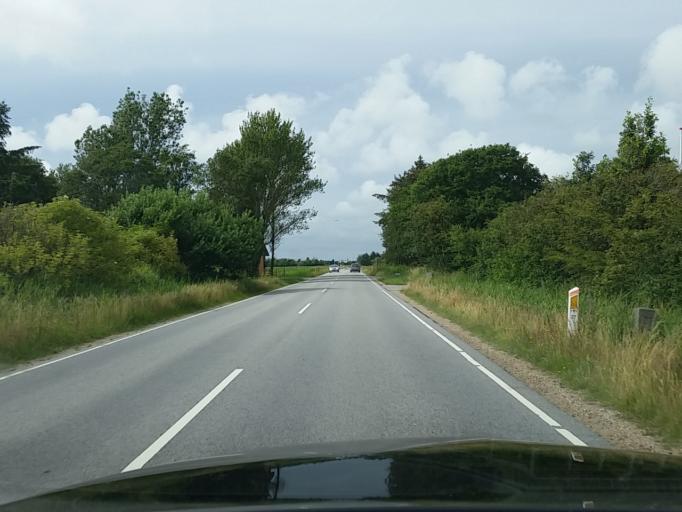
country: DK
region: South Denmark
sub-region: Varde Kommune
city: Oksbol
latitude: 55.7967
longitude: 8.2330
